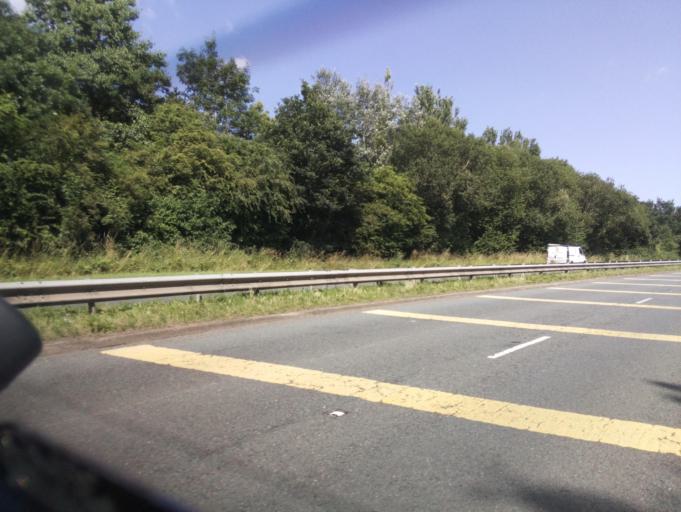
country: GB
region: England
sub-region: Worcestershire
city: Bromsgrove
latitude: 52.3345
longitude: -2.0423
